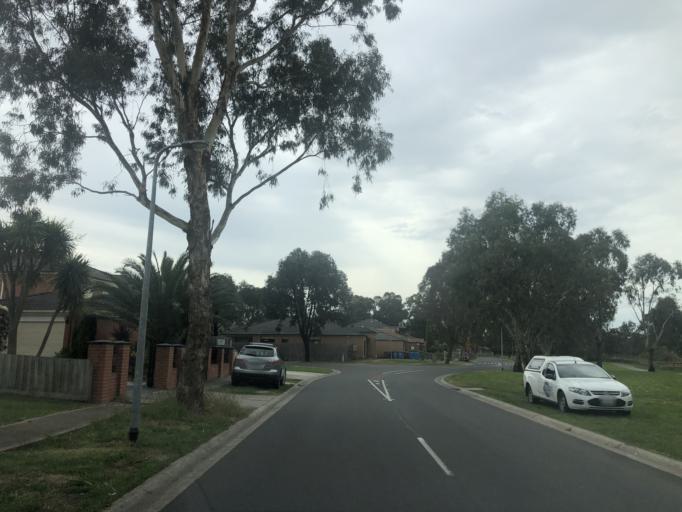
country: AU
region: Victoria
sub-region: Casey
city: Hallam
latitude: -38.0023
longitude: 145.2880
